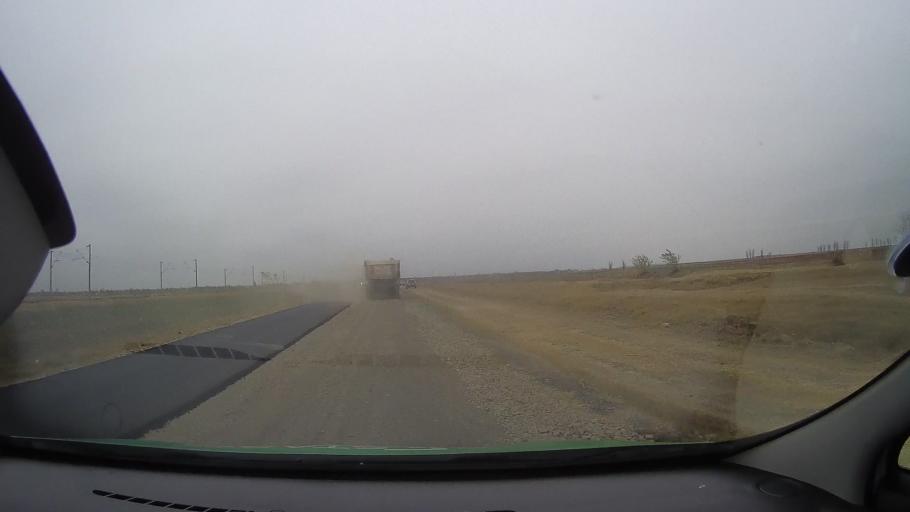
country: RO
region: Braila
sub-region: Comuna Baraganul
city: Baraganul
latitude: 44.8000
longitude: 27.5280
